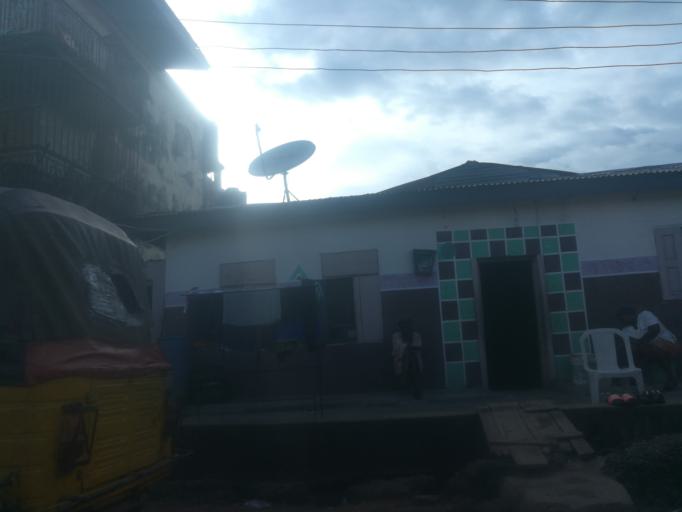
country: NG
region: Lagos
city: Somolu
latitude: 6.5401
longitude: 3.3856
